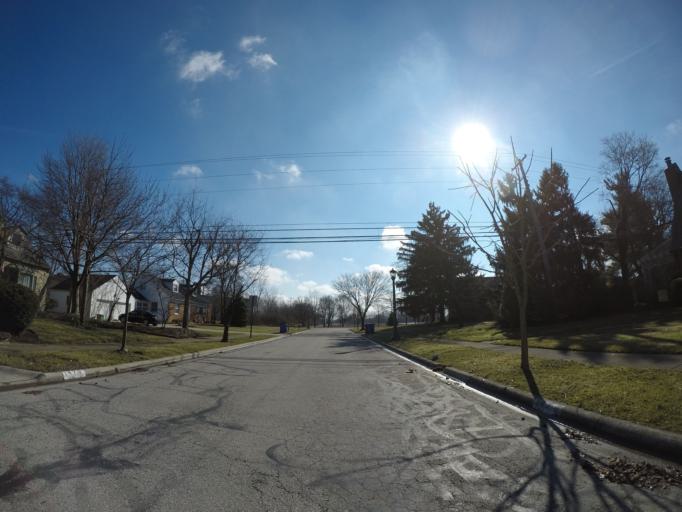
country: US
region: Ohio
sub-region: Franklin County
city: Upper Arlington
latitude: 40.0042
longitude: -83.0490
